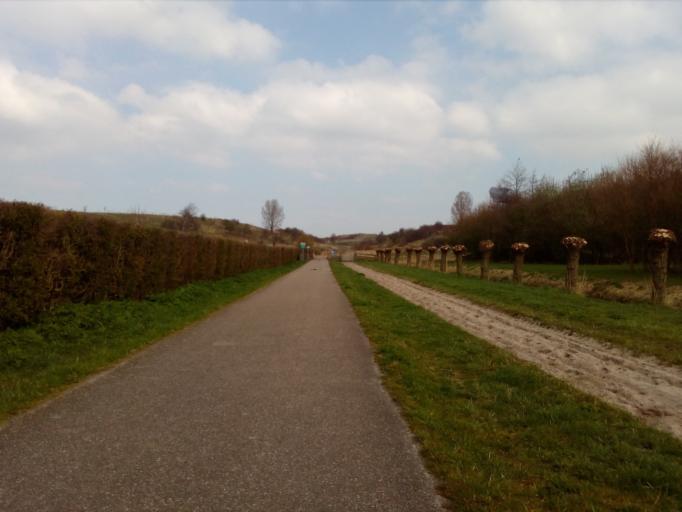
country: NL
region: South Holland
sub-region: Gemeente Zoetermeer
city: Zoetermeer
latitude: 52.0677
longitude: 4.4512
